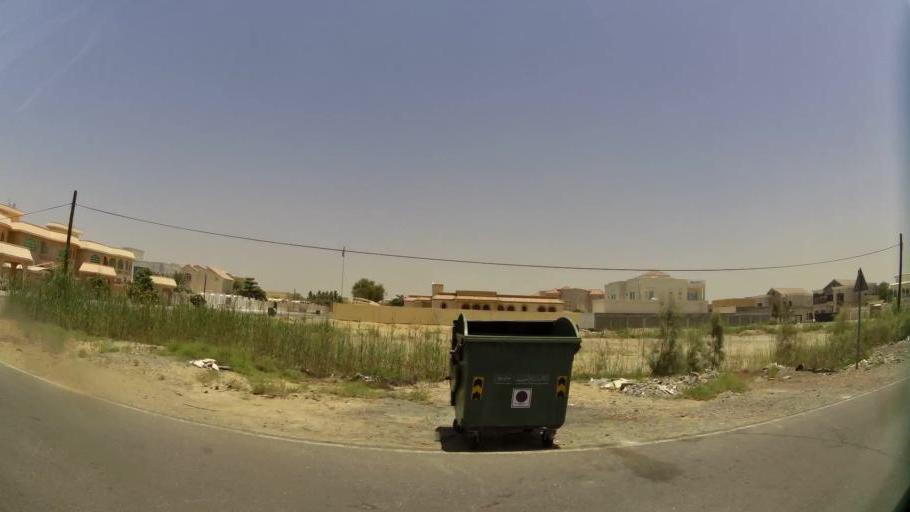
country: AE
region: Ajman
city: Ajman
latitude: 25.4145
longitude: 55.4911
